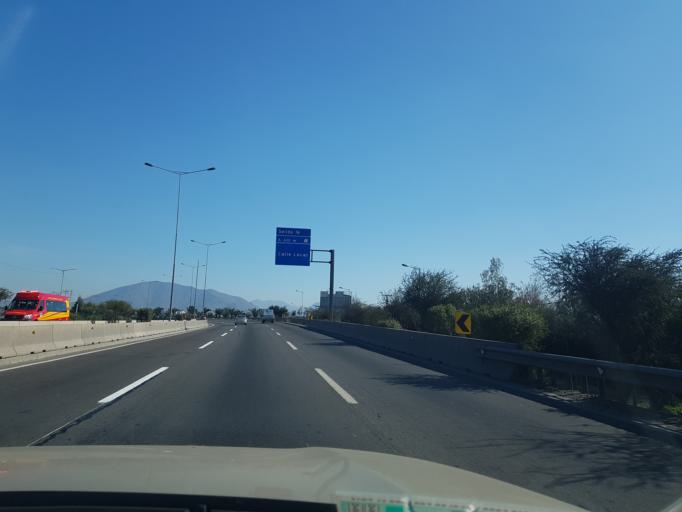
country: CL
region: Santiago Metropolitan
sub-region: Provincia de Santiago
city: Lo Prado
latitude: -33.4039
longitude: -70.7810
